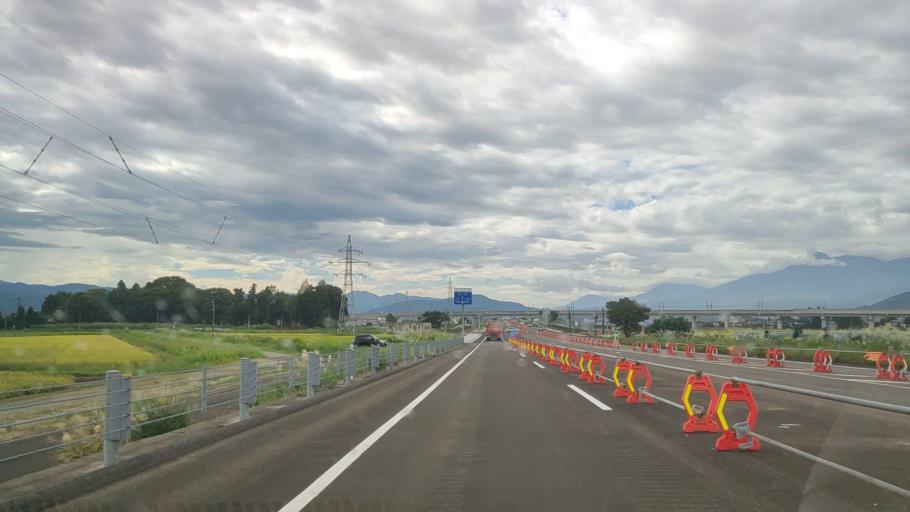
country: JP
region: Niigata
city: Joetsu
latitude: 37.0745
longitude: 138.2651
